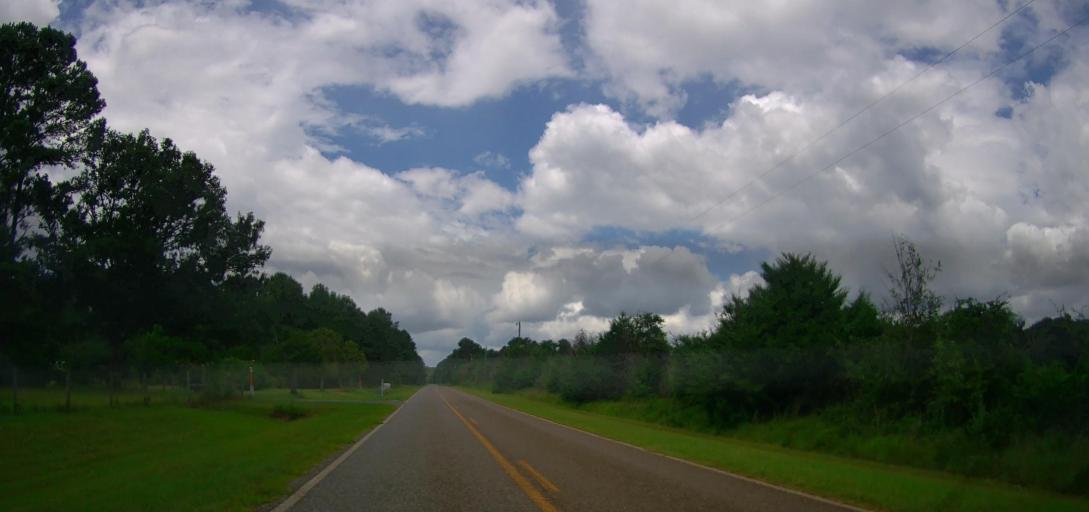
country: US
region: Georgia
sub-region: Pulaski County
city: Hawkinsville
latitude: 32.3440
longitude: -83.5580
